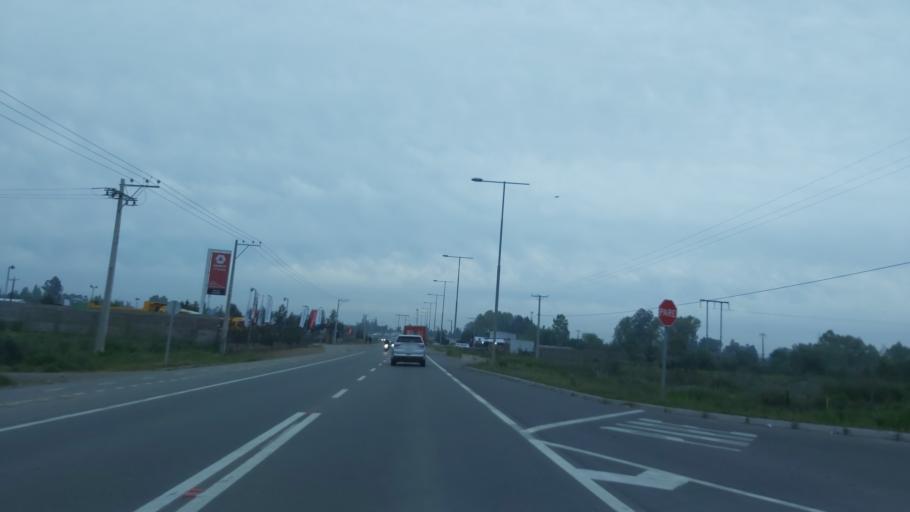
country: CL
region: Maule
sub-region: Provincia de Linares
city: Linares
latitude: -35.8350
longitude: -71.6212
